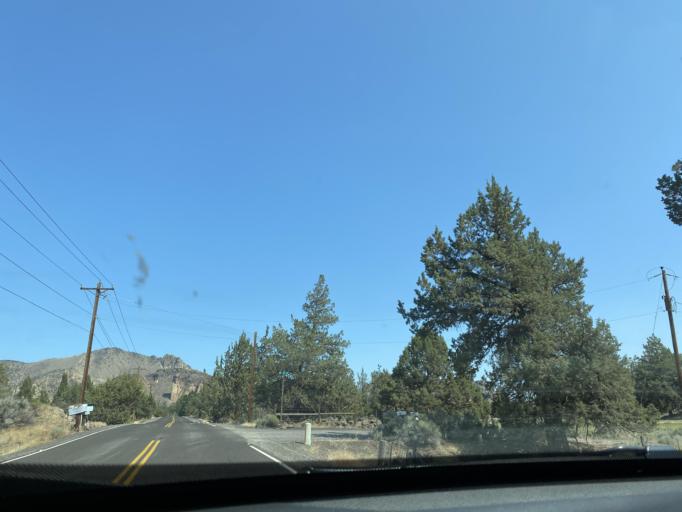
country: US
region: Oregon
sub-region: Deschutes County
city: Terrebonne
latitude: 44.3704
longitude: -121.1709
